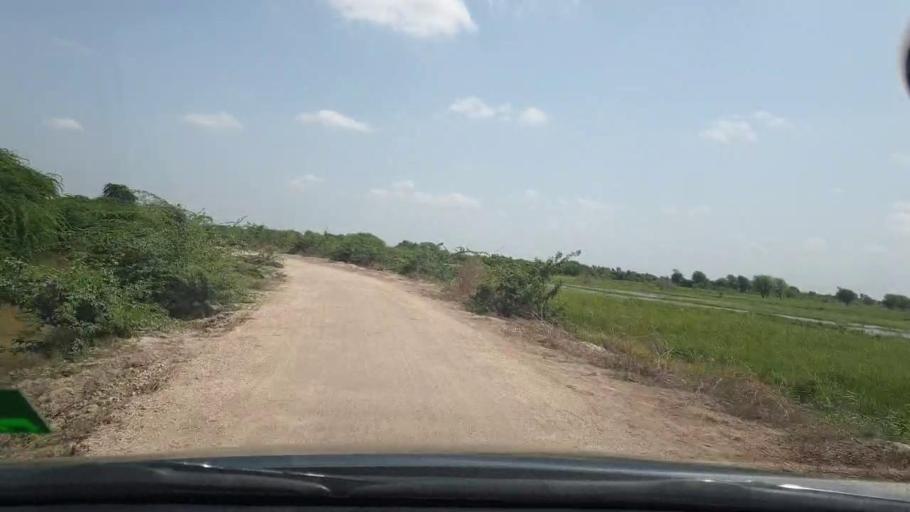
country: PK
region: Sindh
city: Tando Bago
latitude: 24.8787
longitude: 69.0968
